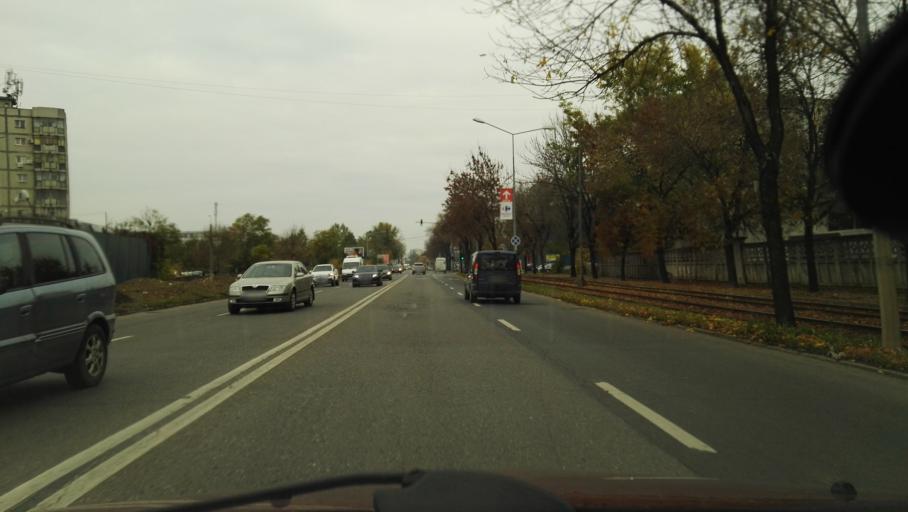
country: RO
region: Bucuresti
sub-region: Municipiul Bucuresti
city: Bucuresti
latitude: 44.4130
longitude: 26.0815
